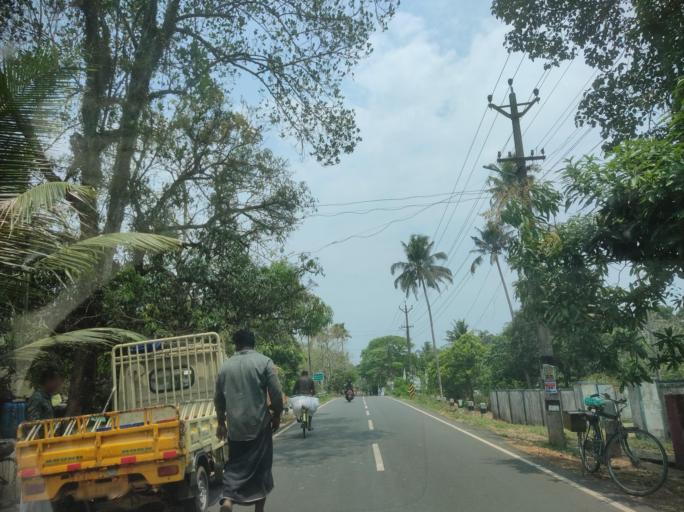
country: IN
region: Kerala
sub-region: Alappuzha
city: Vayalar
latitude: 9.7055
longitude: 76.3253
